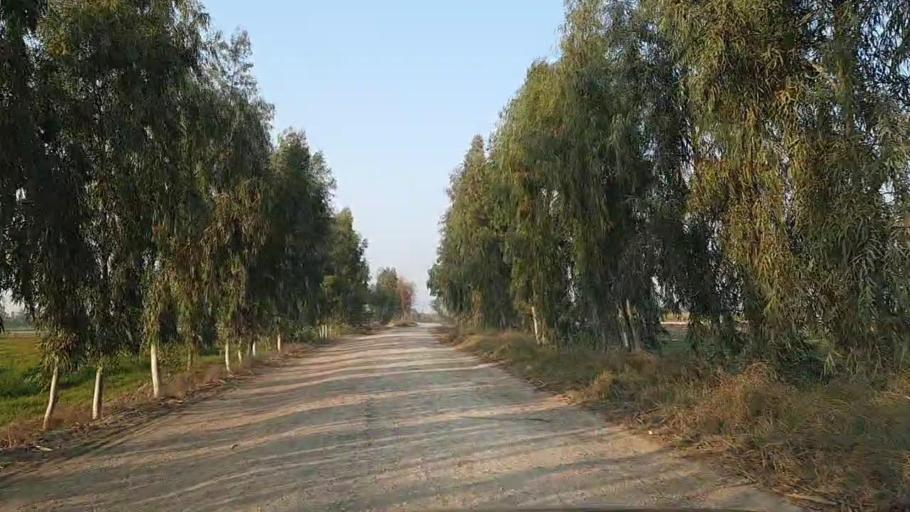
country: PK
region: Sindh
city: Daur
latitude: 26.4269
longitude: 68.3936
